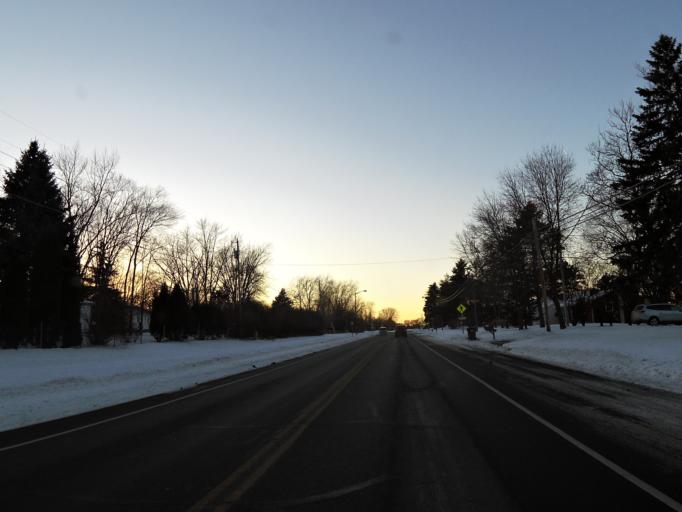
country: US
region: Minnesota
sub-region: Dakota County
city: Rosemount
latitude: 44.7392
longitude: -93.1503
